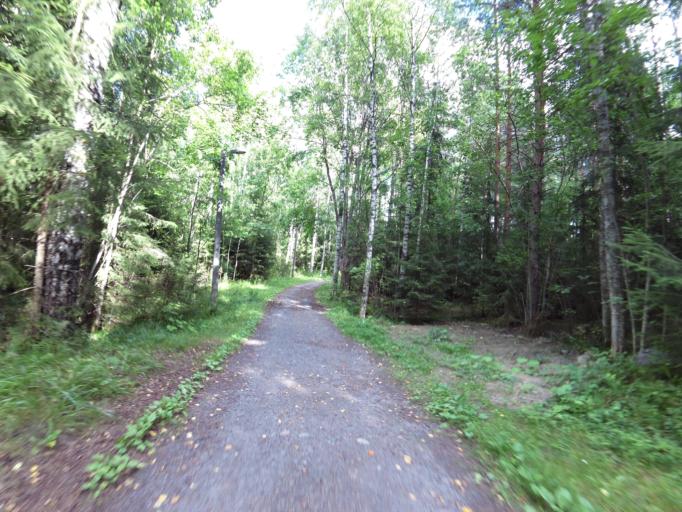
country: FI
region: Pirkanmaa
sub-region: Tampere
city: Yloejaervi
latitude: 61.5121
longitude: 23.6135
